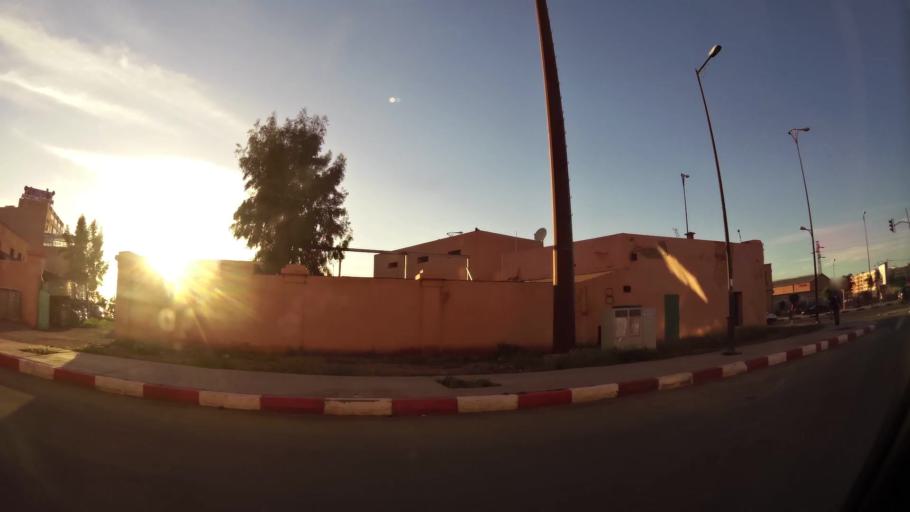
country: MA
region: Marrakech-Tensift-Al Haouz
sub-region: Marrakech
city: Marrakesh
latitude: 31.6262
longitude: -8.0282
